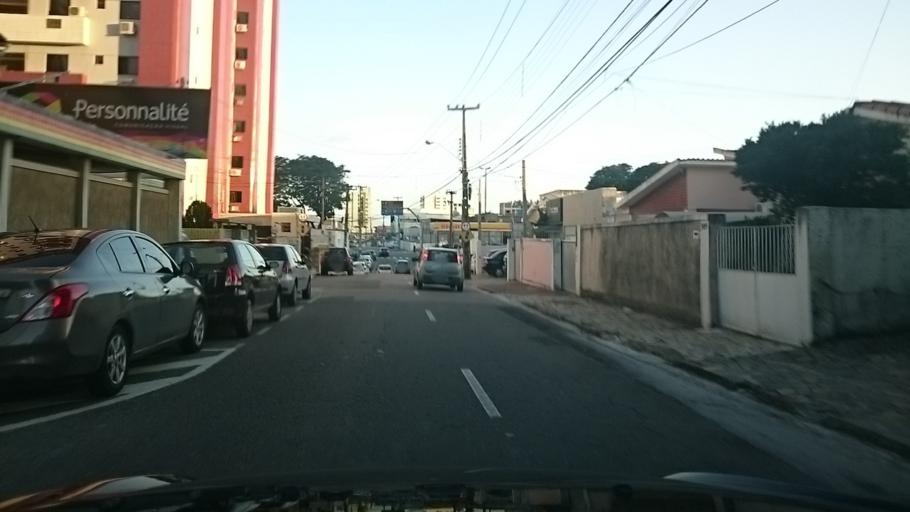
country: BR
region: Paraiba
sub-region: Joao Pessoa
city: Joao Pessoa
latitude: -7.1184
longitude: -34.8370
